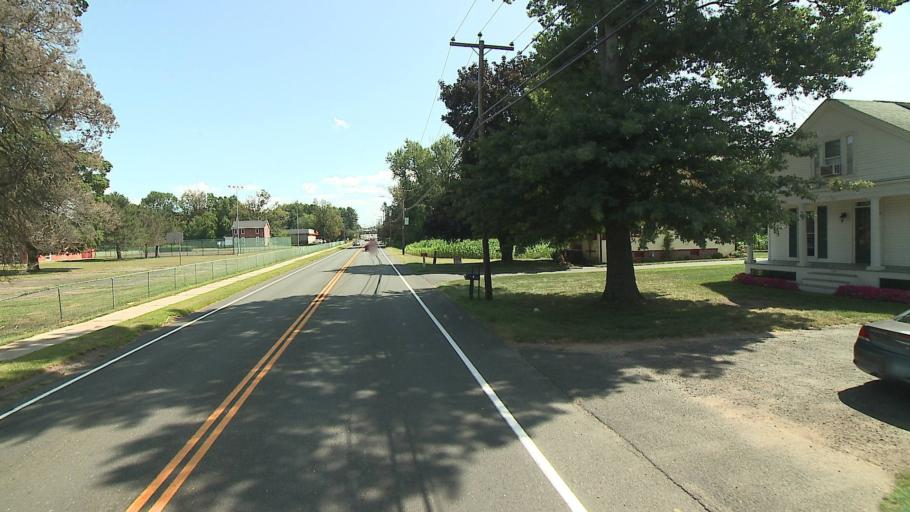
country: US
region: Connecticut
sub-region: Hartford County
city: Windsor Locks
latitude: 41.9297
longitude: -72.6138
